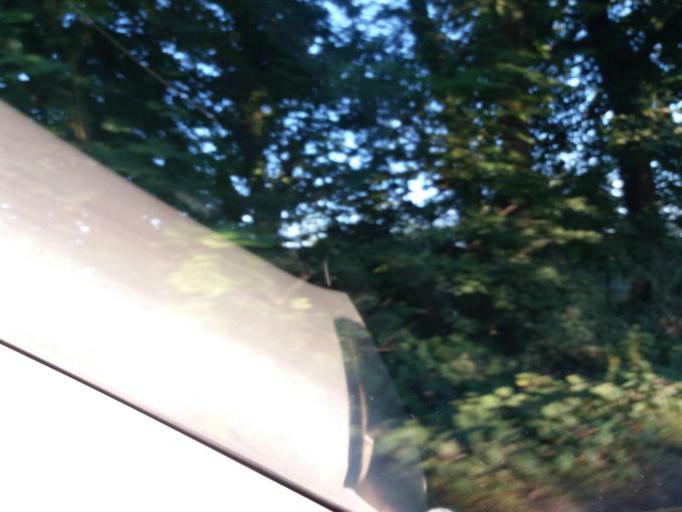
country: IE
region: Leinster
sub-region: Dublin City
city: Finglas
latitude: 53.4485
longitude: -6.3318
